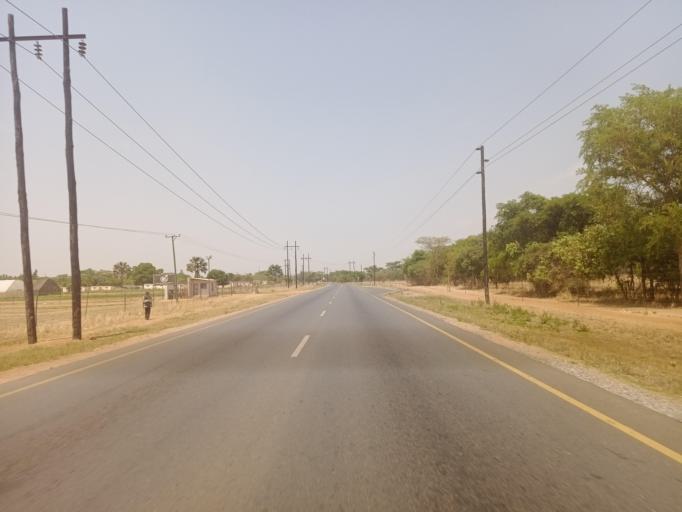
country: ZM
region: Lusaka
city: Lusaka
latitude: -15.2809
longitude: 28.3922
